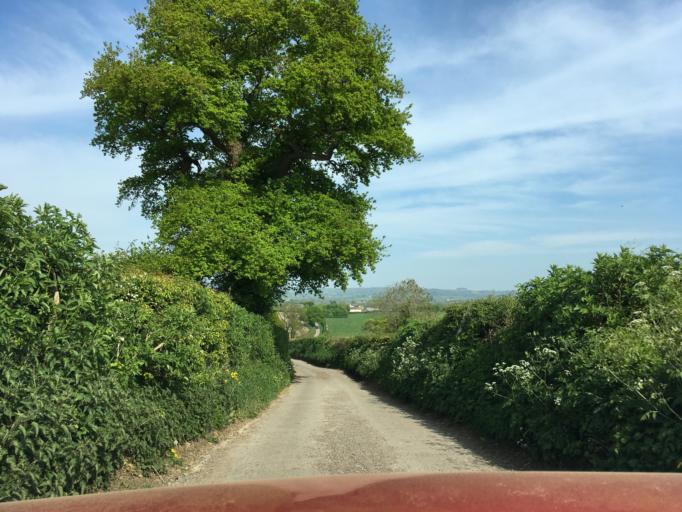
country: GB
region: England
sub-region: South Gloucestershire
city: Charfield
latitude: 51.6150
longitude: -2.4058
